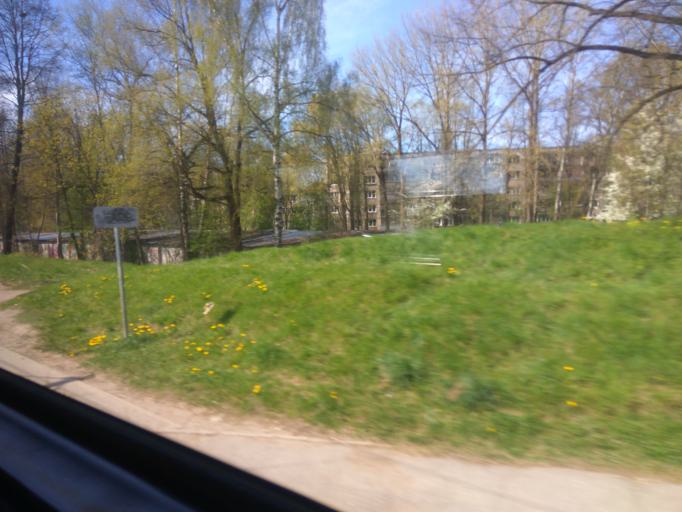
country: LV
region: Riga
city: Riga
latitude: 56.9263
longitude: 24.0781
